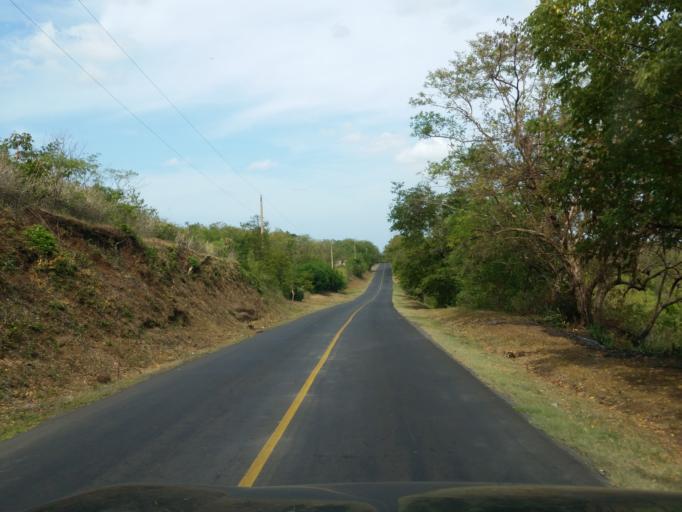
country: NI
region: Managua
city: San Rafael del Sur
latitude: 11.8990
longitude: -86.3938
